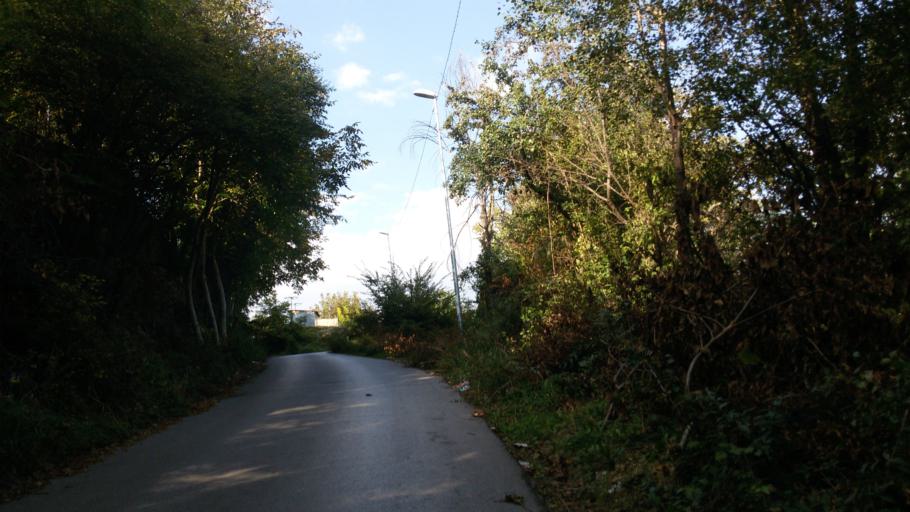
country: RS
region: Central Serbia
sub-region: Belgrade
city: Rakovica
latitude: 44.7368
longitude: 20.4285
